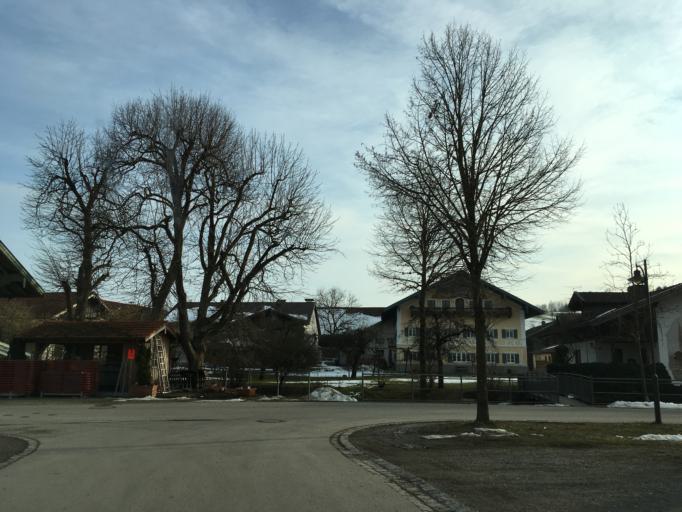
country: DE
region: Bavaria
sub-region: Upper Bavaria
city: Sochtenau
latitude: 47.9313
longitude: 12.2307
